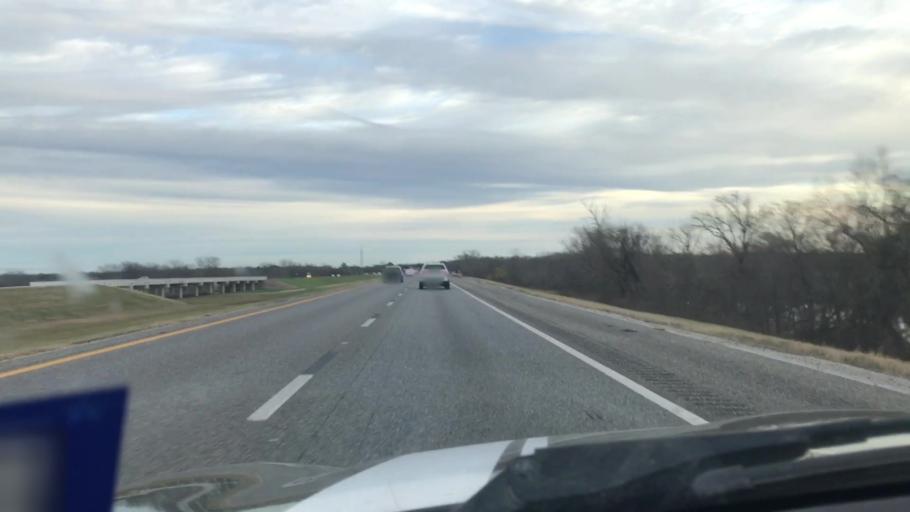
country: US
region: Texas
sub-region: Waller County
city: Hempstead
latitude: 30.1299
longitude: -96.1582
